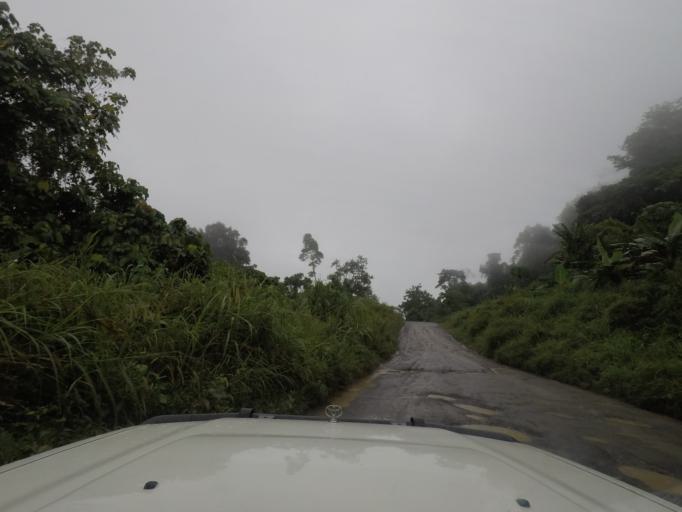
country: PG
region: Madang
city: Madang
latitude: -5.4523
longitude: 145.5079
